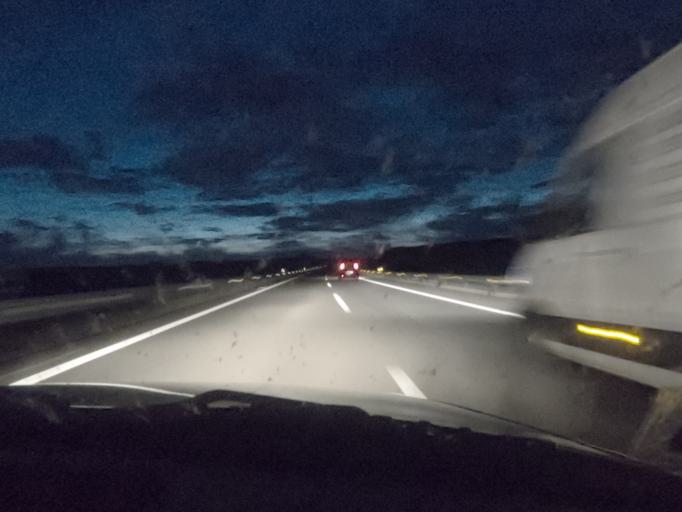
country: ES
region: Extremadura
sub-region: Provincia de Caceres
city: Morcillo
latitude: 39.9825
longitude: -6.4186
